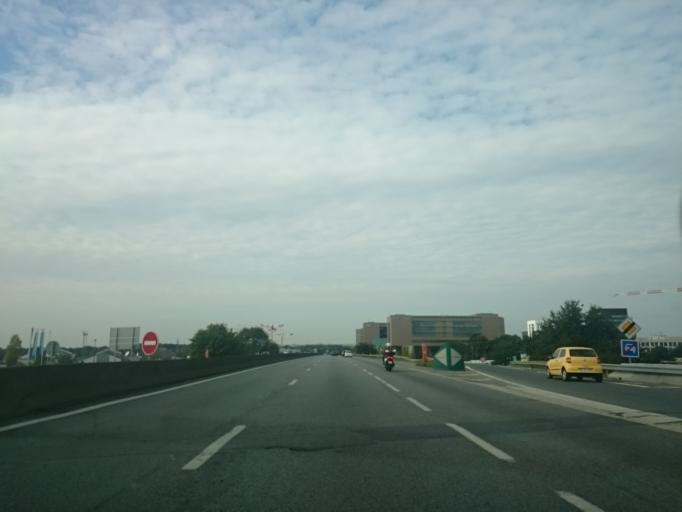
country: FR
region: Brittany
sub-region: Departement d'Ille-et-Vilaine
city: Saint-Jacques-de-la-Lande
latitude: 48.0890
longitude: -1.7031
